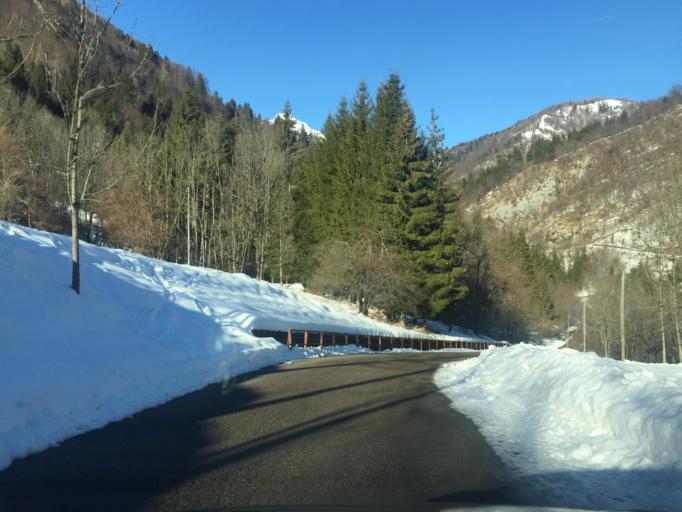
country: IT
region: Friuli Venezia Giulia
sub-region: Provincia di Udine
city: Lauco
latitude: 46.4414
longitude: 12.9492
